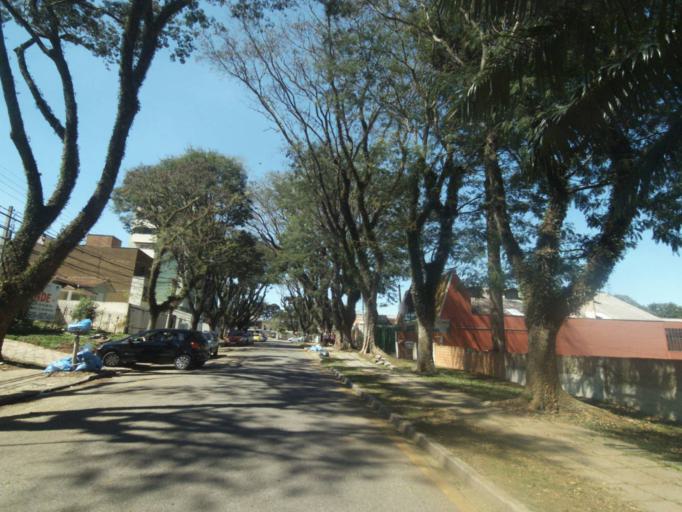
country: BR
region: Parana
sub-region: Curitiba
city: Curitiba
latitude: -25.4053
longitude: -49.2417
